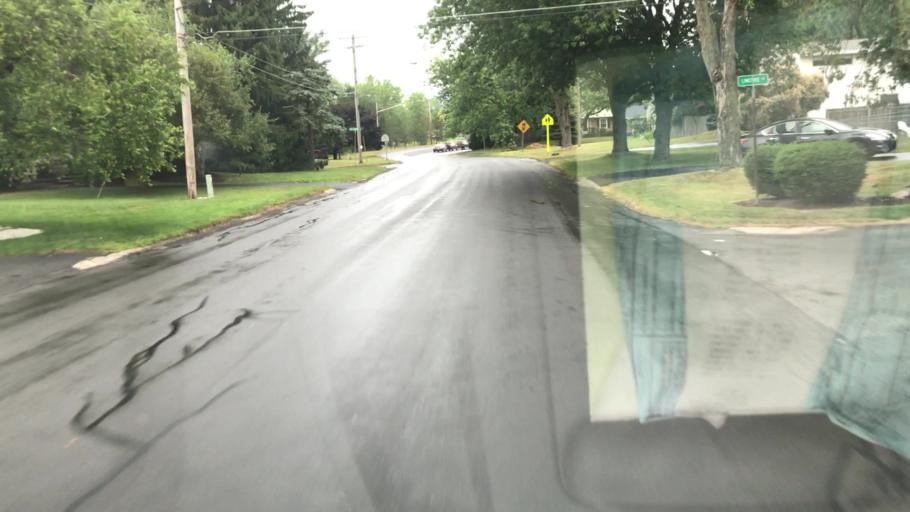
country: US
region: New York
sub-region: Onondaga County
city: Liverpool
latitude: 43.1399
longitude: -76.2110
